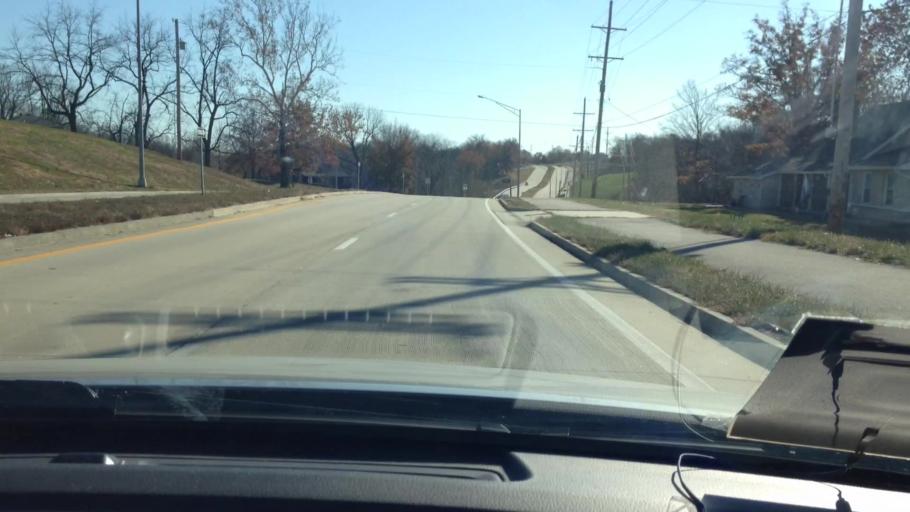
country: US
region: Missouri
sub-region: Platte County
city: Weatherby Lake
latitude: 39.2180
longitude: -94.7315
